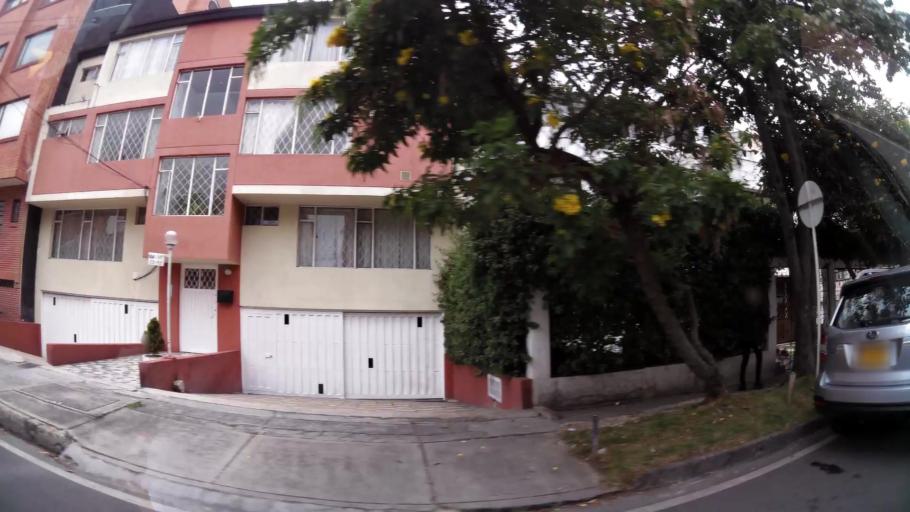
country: CO
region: Bogota D.C.
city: Barrio San Luis
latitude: 4.7260
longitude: -74.0383
